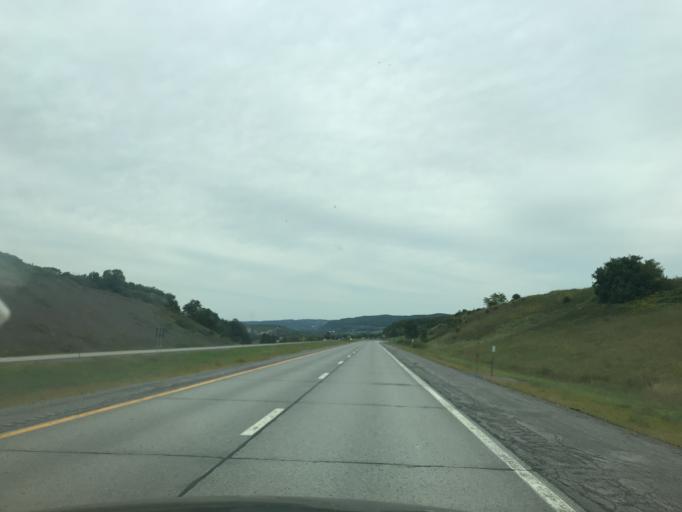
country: US
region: New York
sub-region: Schoharie County
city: Cobleskill
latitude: 42.6771
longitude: -74.4263
